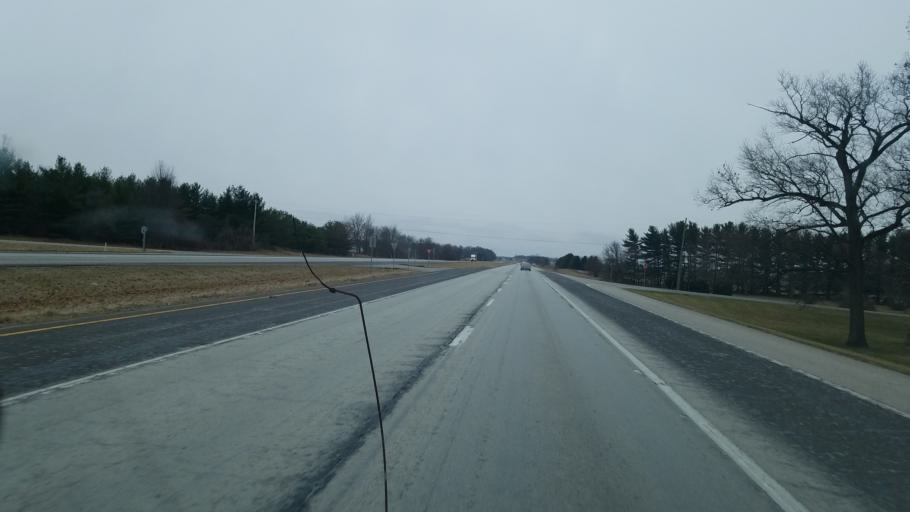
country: US
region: Indiana
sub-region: Fulton County
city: Rochester
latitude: 41.0696
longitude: -86.2401
